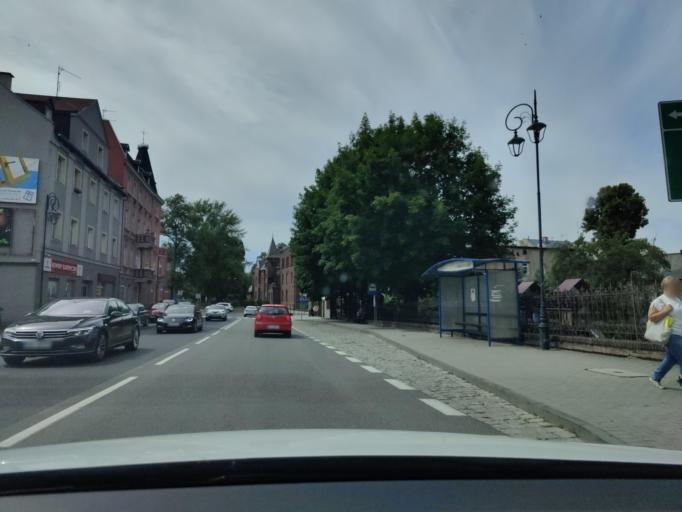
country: PL
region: Opole Voivodeship
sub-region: Powiat nyski
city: Glucholazy
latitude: 50.3134
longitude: 17.3844
